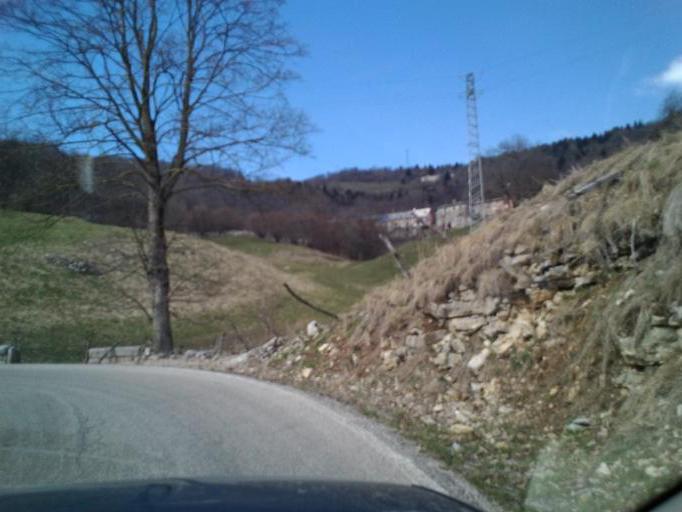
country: IT
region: Veneto
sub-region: Provincia di Verona
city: Erbezzo
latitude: 45.6501
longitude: 11.0062
